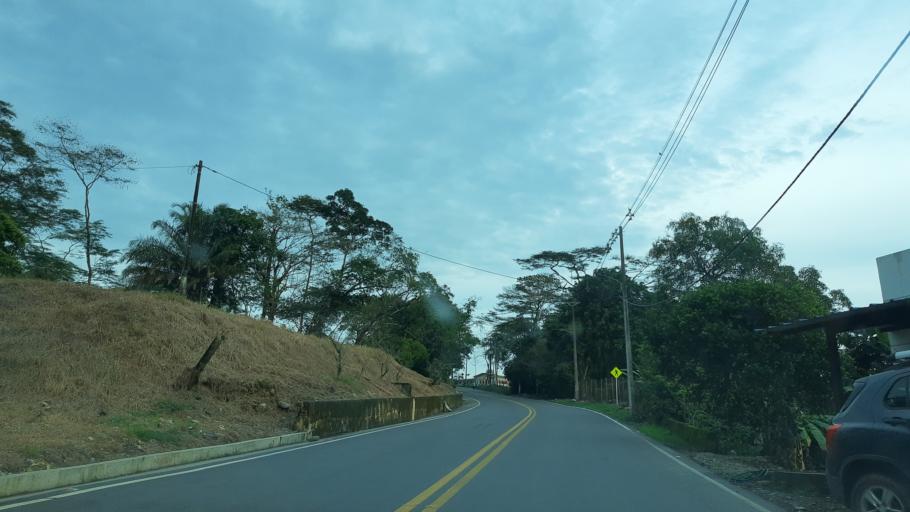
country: CO
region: Casanare
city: Sabanalarga
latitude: 4.8194
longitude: -73.0723
